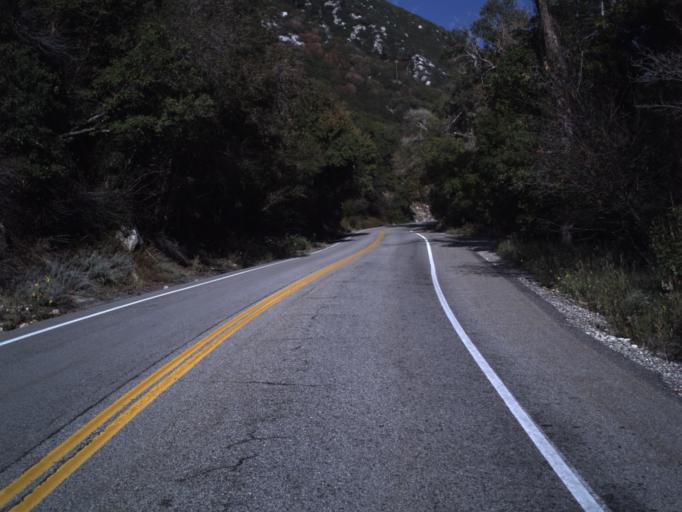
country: US
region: Utah
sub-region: Salt Lake County
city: Granite
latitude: 40.5718
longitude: -111.7492
